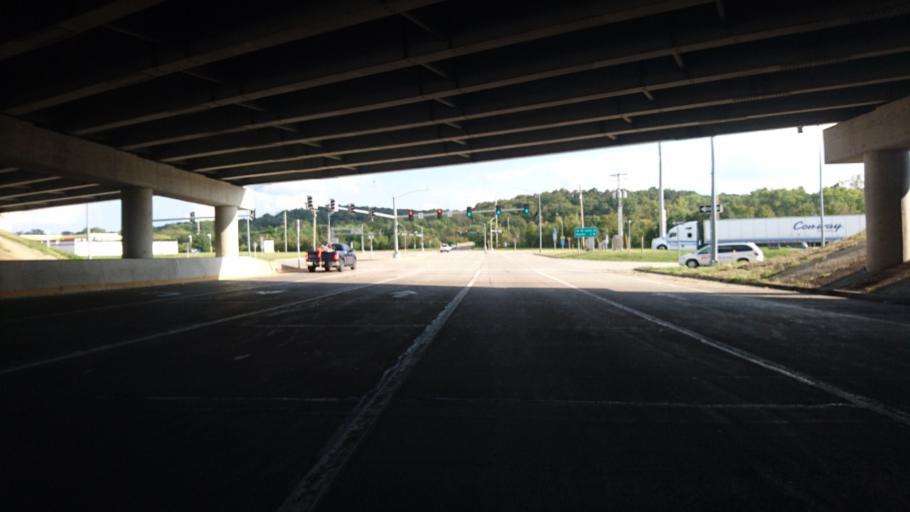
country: US
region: Missouri
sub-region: Saint Louis County
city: Eureka
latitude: 38.5058
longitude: -90.6775
